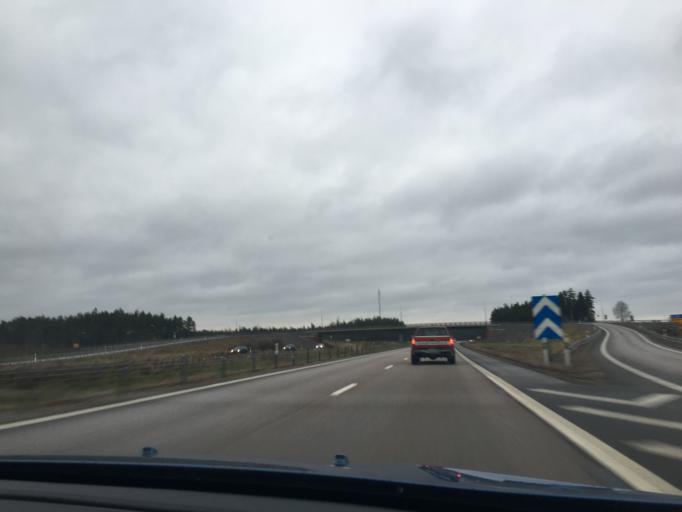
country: SE
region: Uppsala
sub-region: Tierps Kommun
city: Tierp
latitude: 60.4371
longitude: 17.4229
